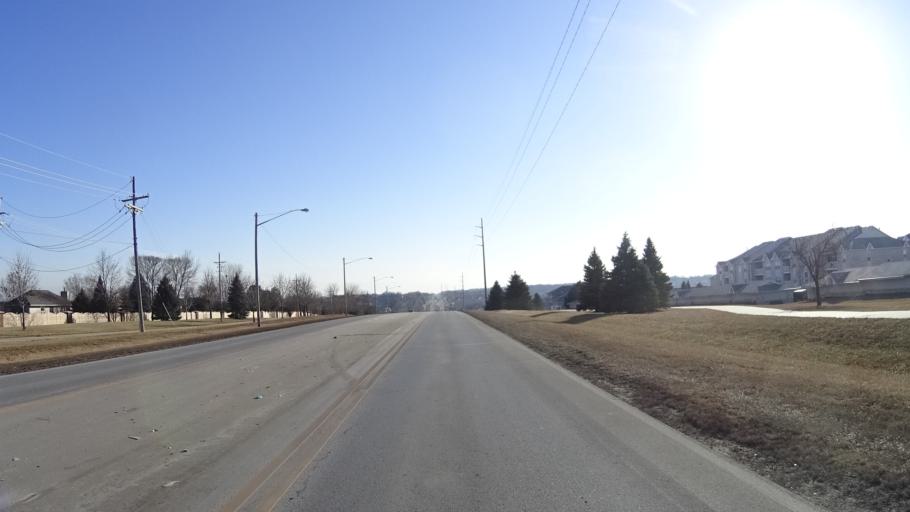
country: US
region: Nebraska
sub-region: Douglas County
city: Bennington
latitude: 41.2976
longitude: -96.1389
